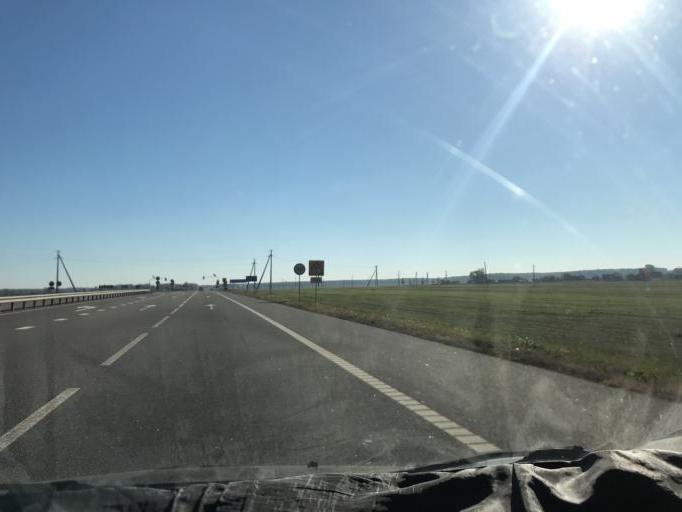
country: BY
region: Mogilev
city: Yalizava
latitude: 53.2235
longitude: 29.0132
